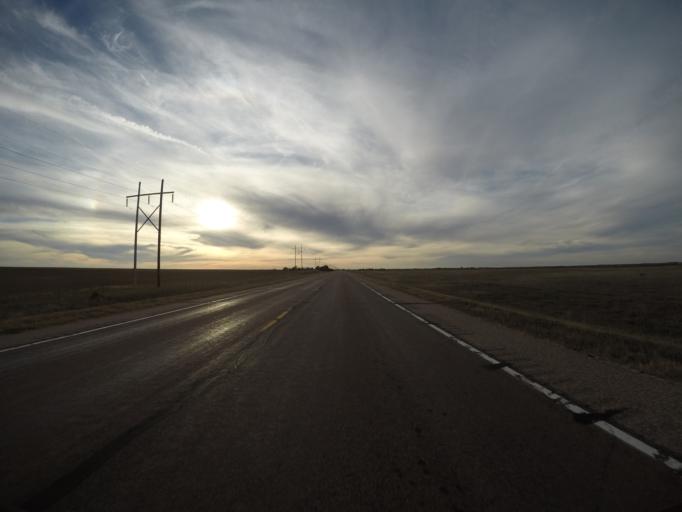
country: US
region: Colorado
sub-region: Yuma County
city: Yuma
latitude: 39.6550
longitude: -102.8122
